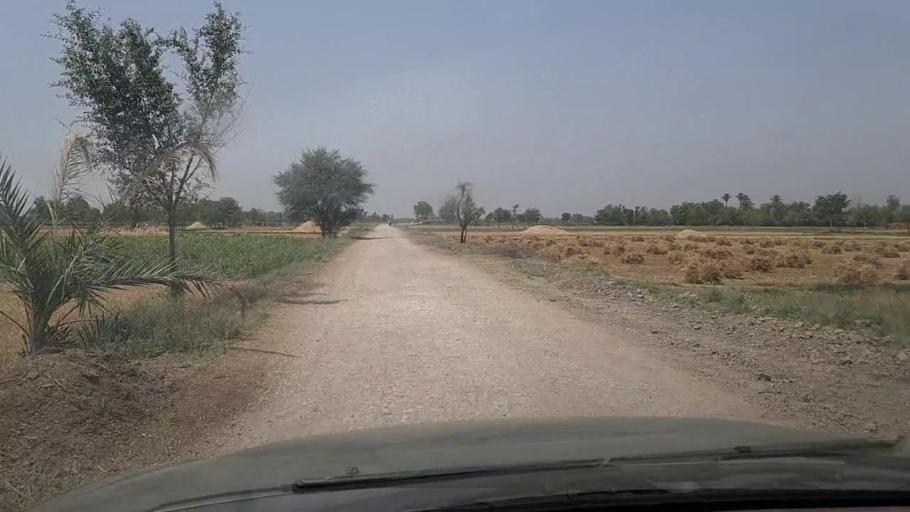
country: PK
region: Sindh
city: Adilpur
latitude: 27.9332
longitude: 69.2650
